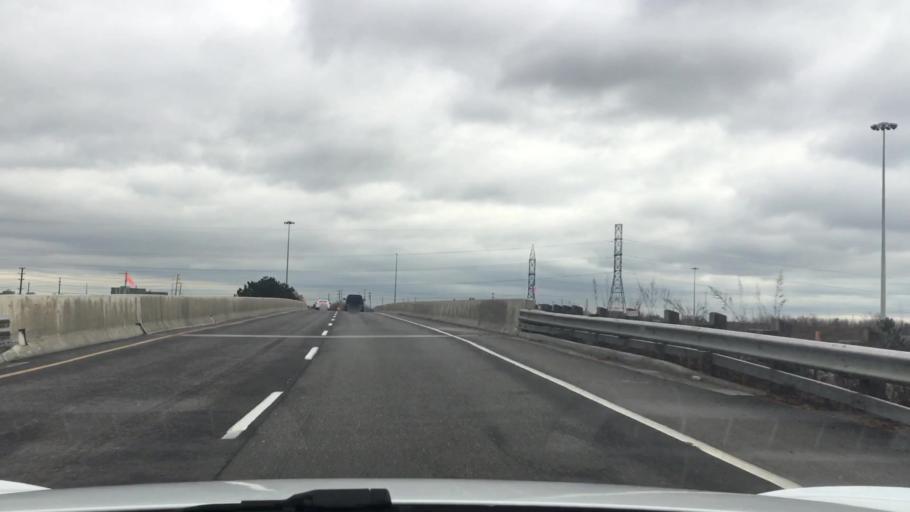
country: CA
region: Ontario
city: Mississauga
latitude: 43.6183
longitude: -79.6334
